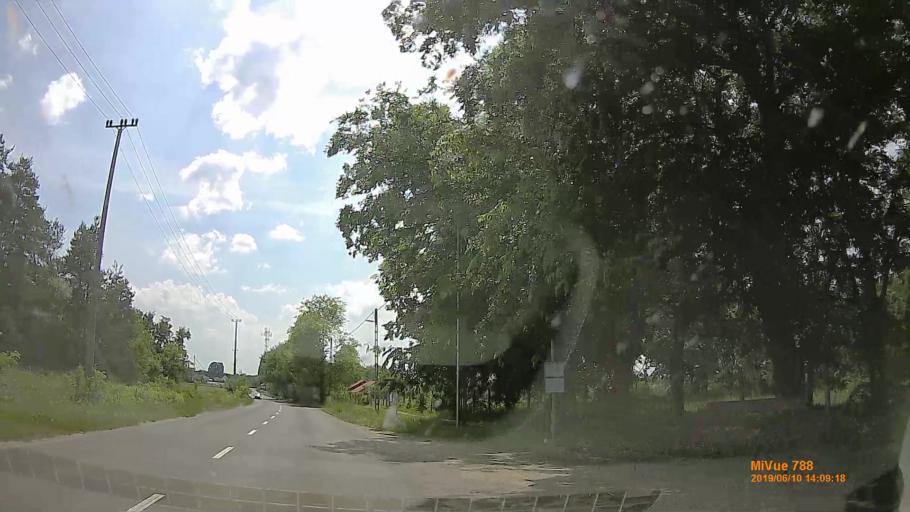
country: HU
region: Pest
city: God
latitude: 47.6824
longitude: 19.1523
